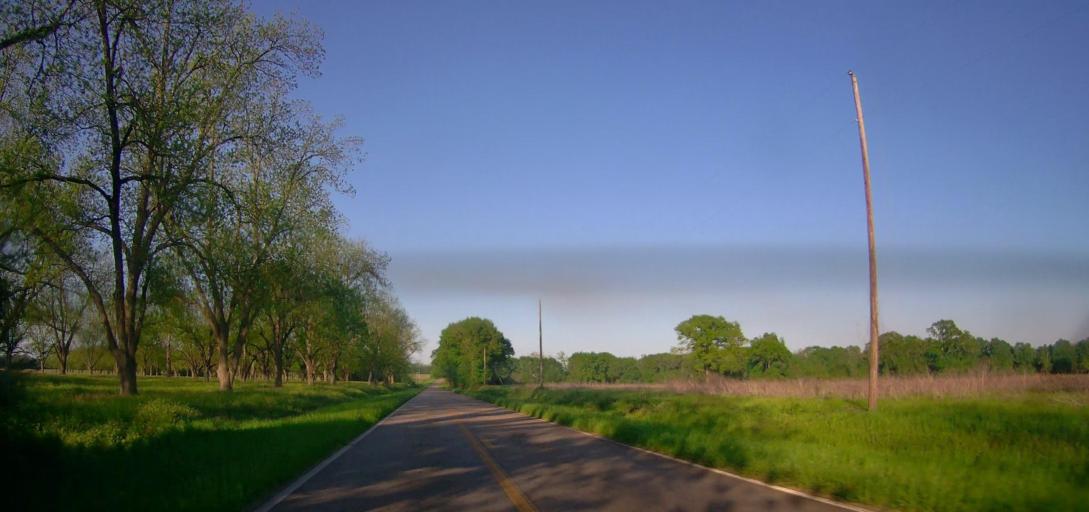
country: US
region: Georgia
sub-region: Macon County
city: Oglethorpe
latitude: 32.3022
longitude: -84.1371
